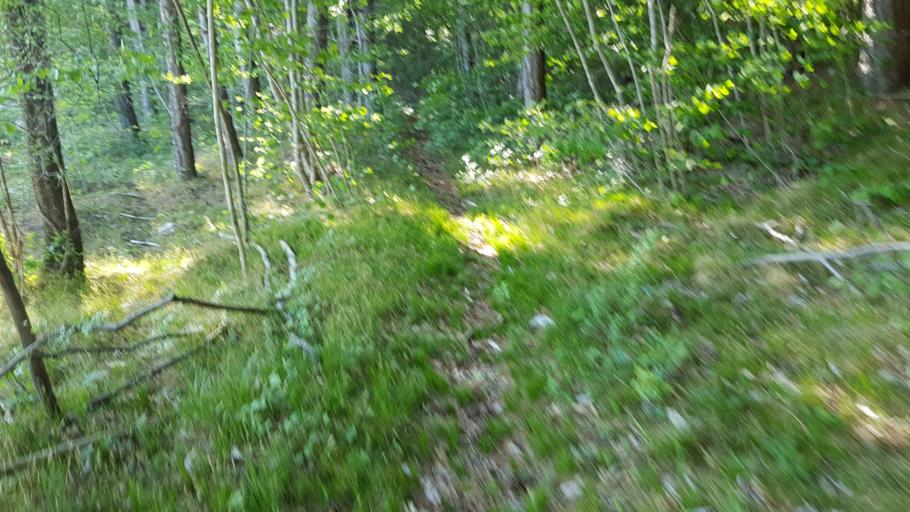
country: IT
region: Trentino-Alto Adige
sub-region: Provincia di Trento
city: Vezzano
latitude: 46.0929
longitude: 11.0020
